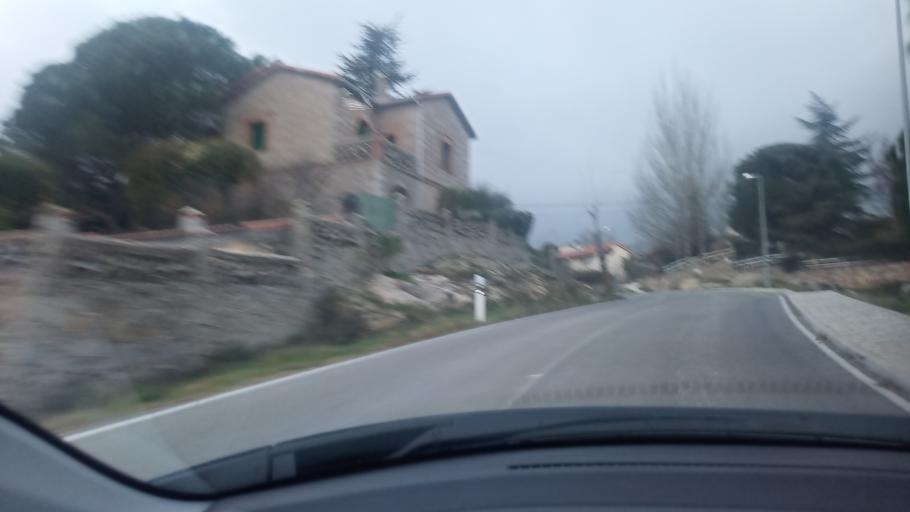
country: ES
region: Madrid
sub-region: Provincia de Madrid
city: Zarzalejo
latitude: 40.5471
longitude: -4.1768
